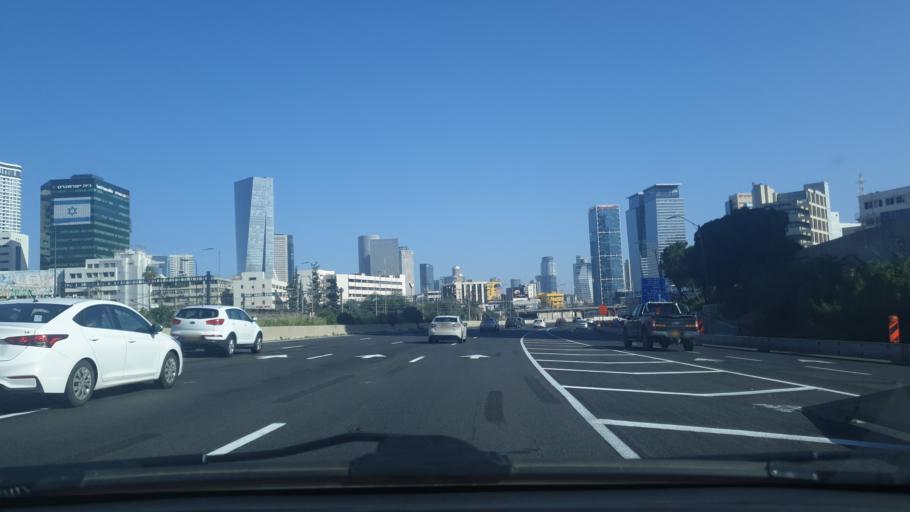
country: IL
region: Tel Aviv
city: Tel Aviv
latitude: 32.0615
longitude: 34.7873
